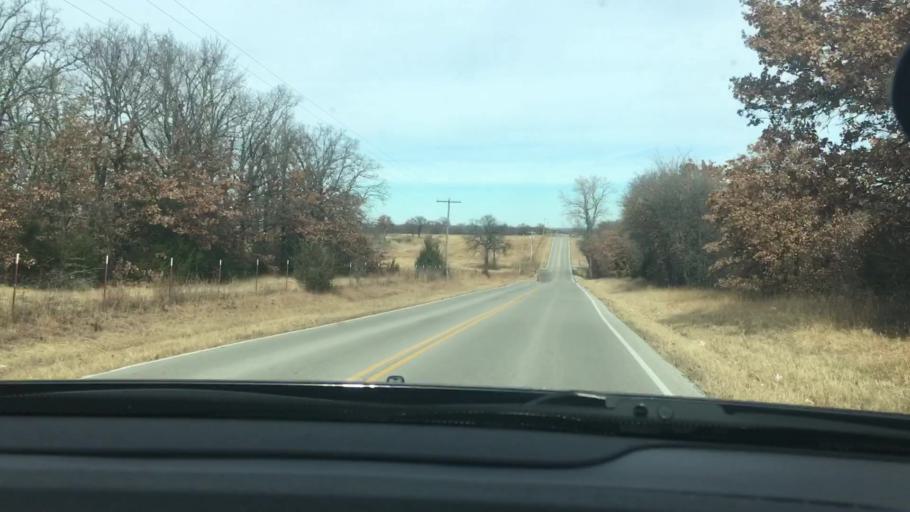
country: US
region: Oklahoma
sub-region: Carter County
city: Ardmore
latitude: 34.1792
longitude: -97.0731
